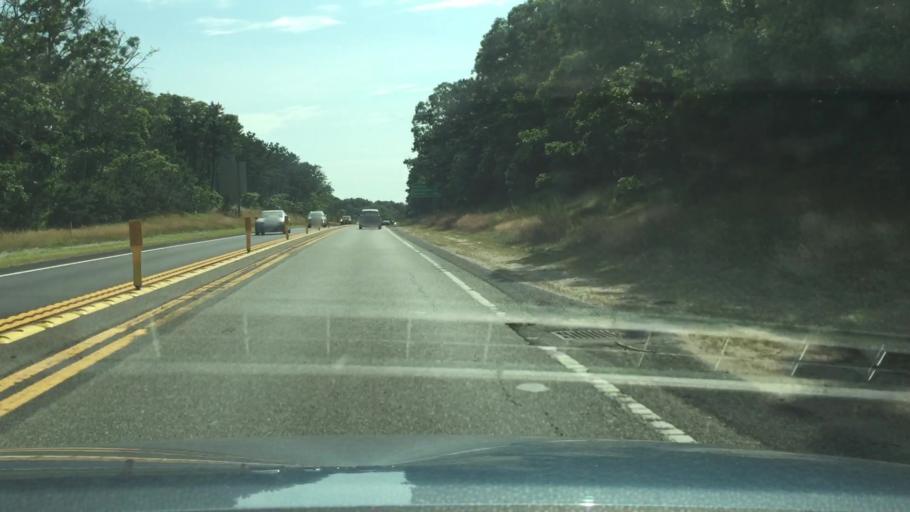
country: US
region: Massachusetts
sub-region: Barnstable County
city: East Harwich
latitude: 41.7186
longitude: -70.0435
